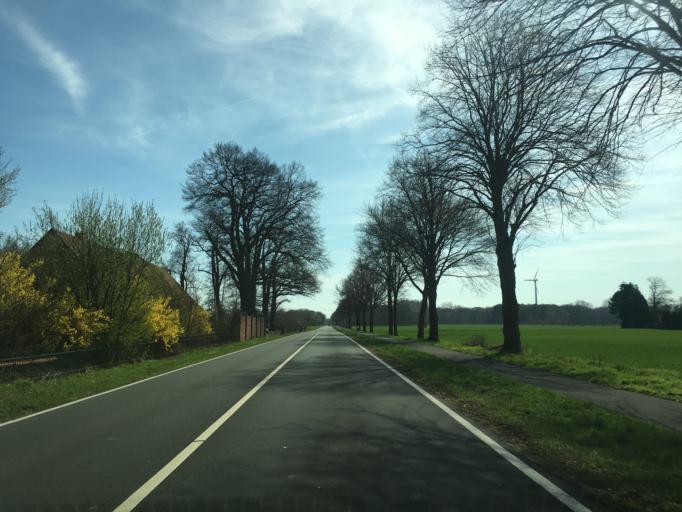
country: DE
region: North Rhine-Westphalia
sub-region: Regierungsbezirk Munster
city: Greven
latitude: 52.0643
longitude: 7.6132
